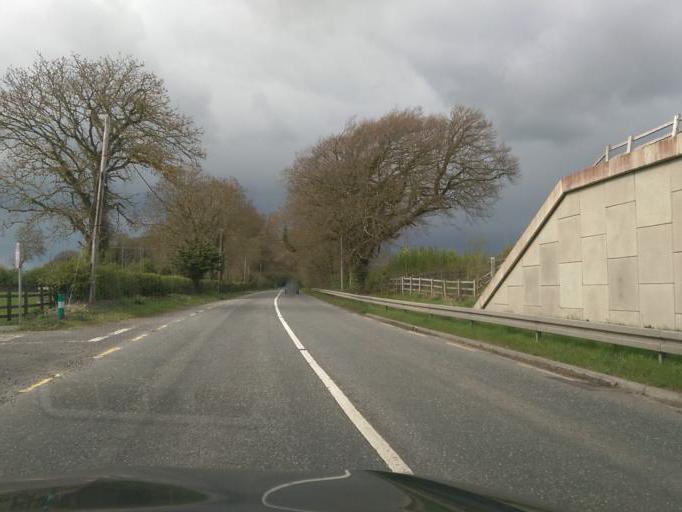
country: IE
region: Leinster
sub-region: An Mhi
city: Dunshaughlin
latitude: 53.5264
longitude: -6.5563
